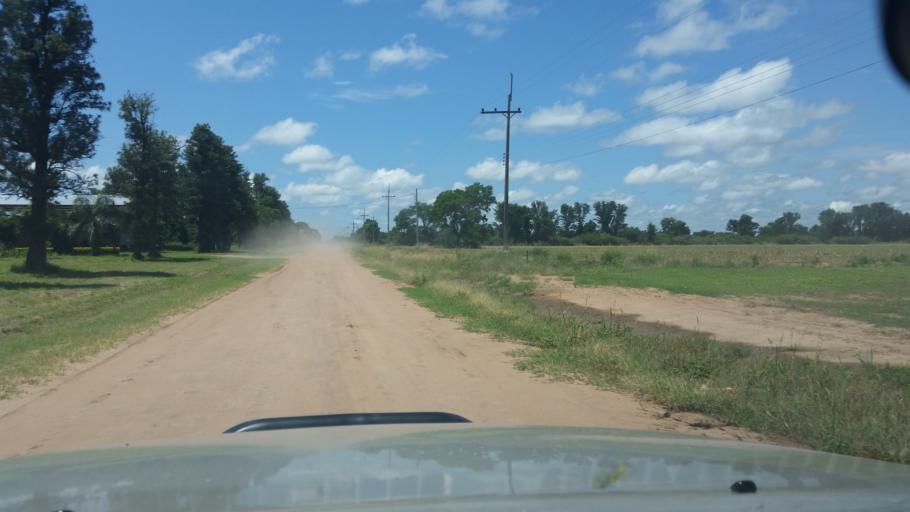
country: PY
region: Boqueron
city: Colonia Neuland
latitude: -22.4384
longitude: -60.3935
